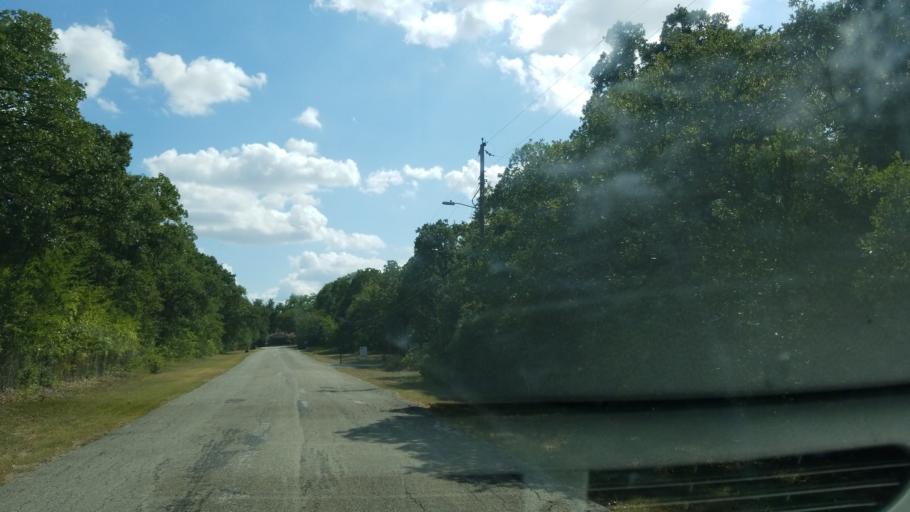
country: US
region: Texas
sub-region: Tarrant County
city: Euless
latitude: 32.8612
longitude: -97.0897
